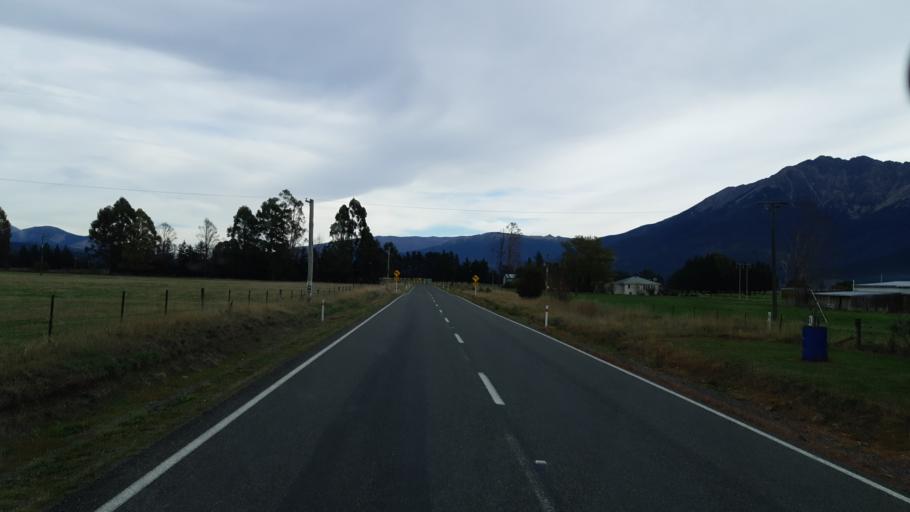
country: NZ
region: Tasman
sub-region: Tasman District
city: Brightwater
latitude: -41.6383
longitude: 173.3160
